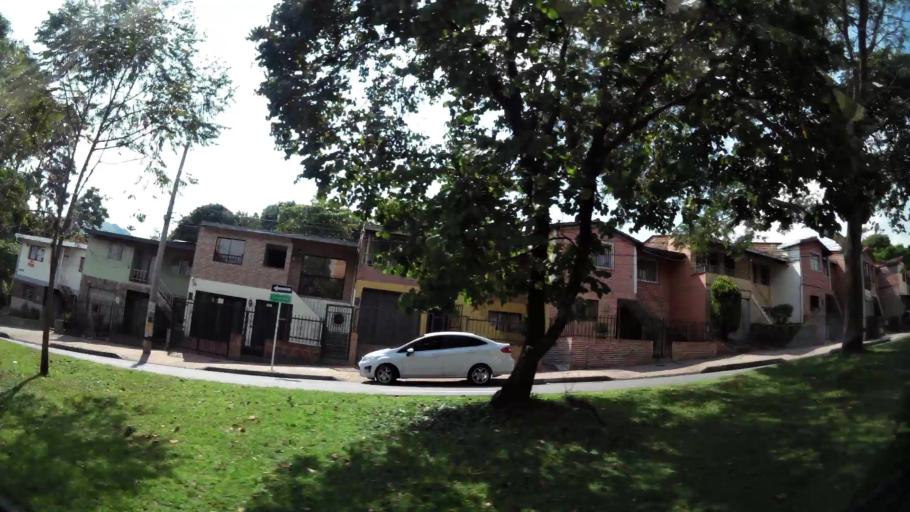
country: CO
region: Antioquia
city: Itagui
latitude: 6.2227
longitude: -75.5978
